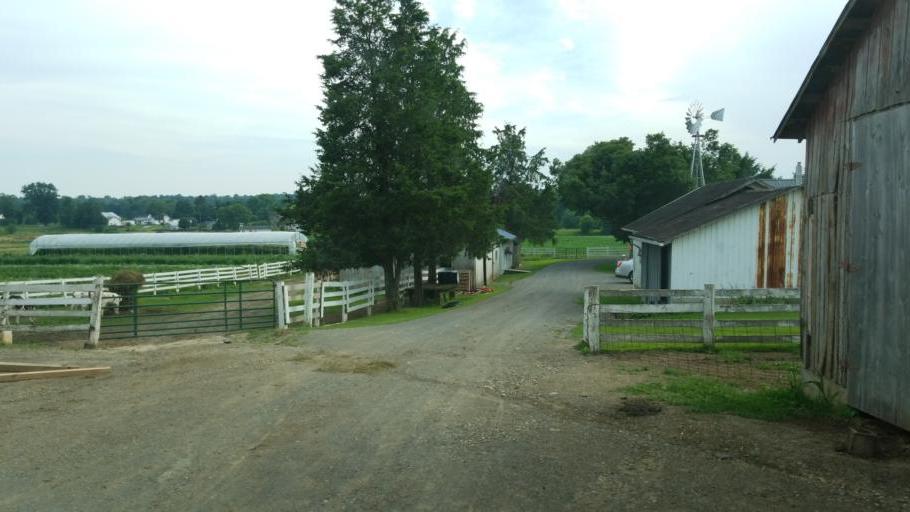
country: US
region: Ohio
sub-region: Knox County
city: Fredericktown
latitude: 40.5477
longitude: -82.6180
